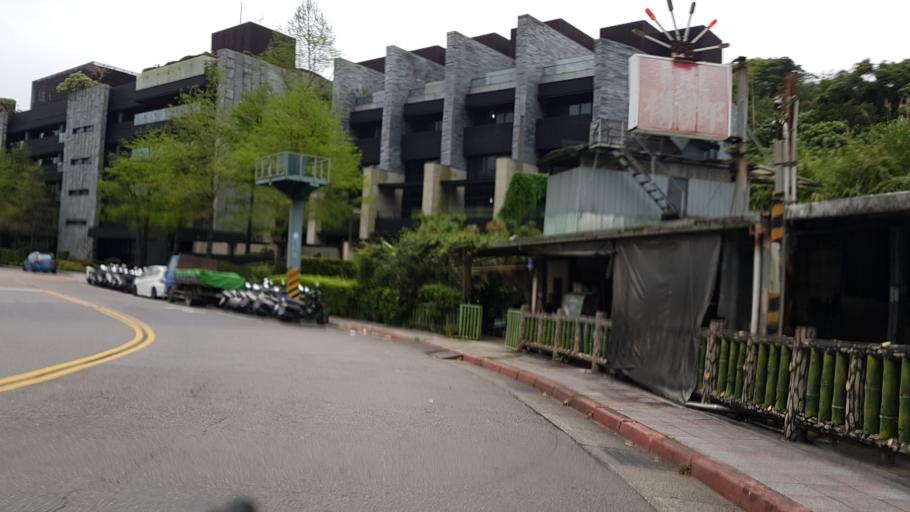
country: TW
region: Taipei
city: Taipei
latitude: 25.0409
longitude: 121.5932
